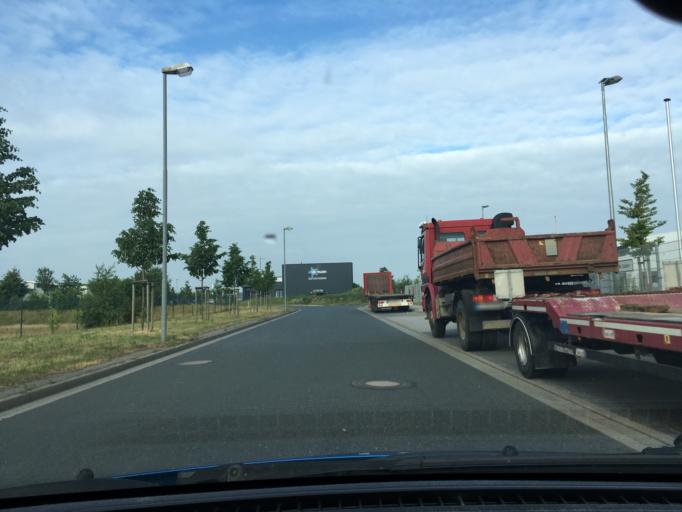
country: DE
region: Lower Saxony
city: Buchholz in der Nordheide
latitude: 53.3239
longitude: 9.8173
